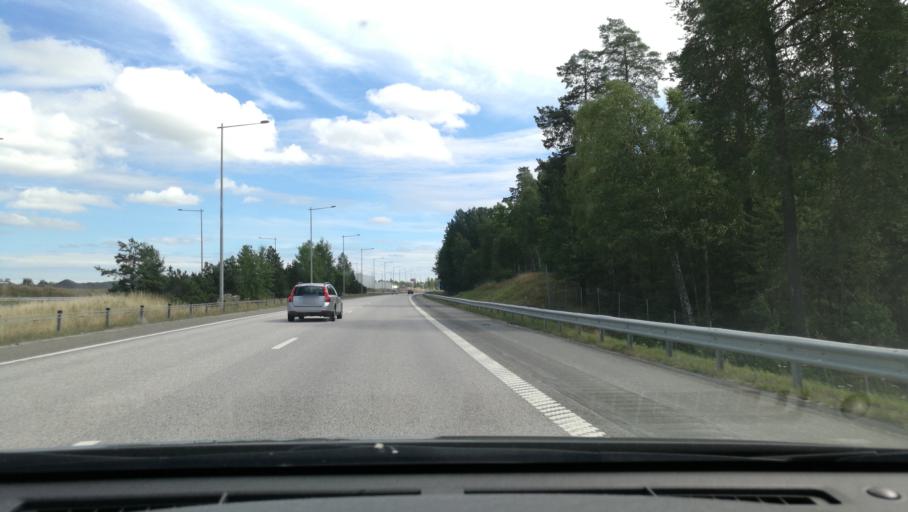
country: SE
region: Stockholm
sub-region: Upplands-Bro Kommun
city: Kungsaengen
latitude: 59.5061
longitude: 17.7281
